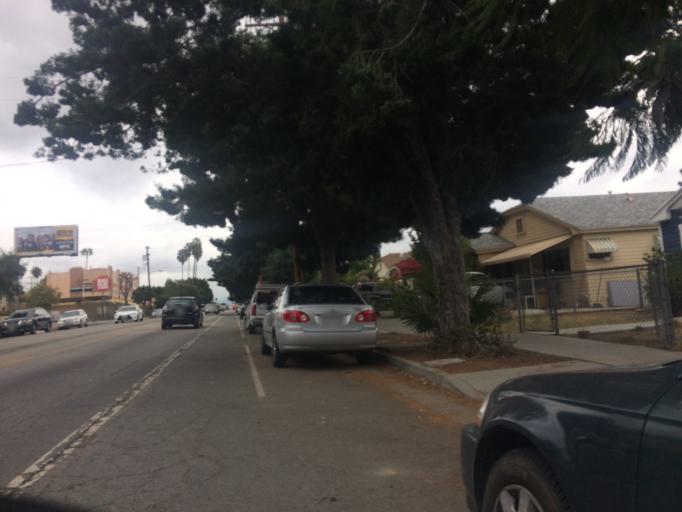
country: US
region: California
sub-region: Los Angeles County
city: Glendale
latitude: 34.1222
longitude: -118.2108
